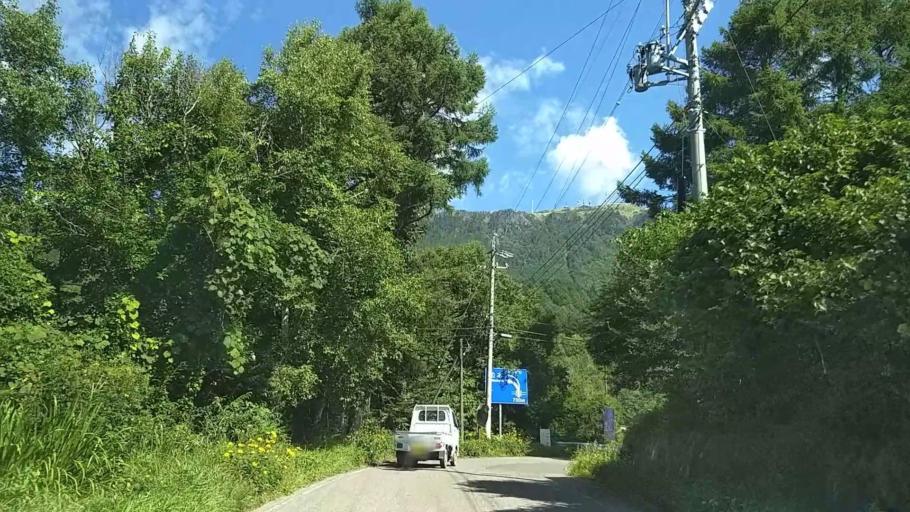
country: JP
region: Nagano
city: Matsumoto
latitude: 36.2080
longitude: 138.1021
